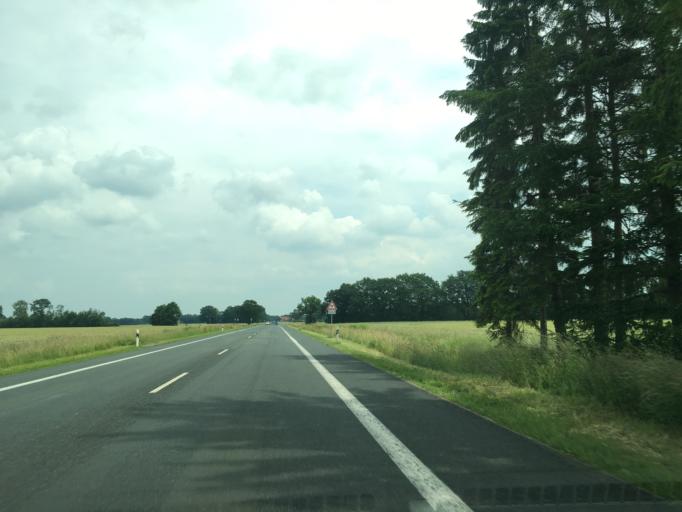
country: DE
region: North Rhine-Westphalia
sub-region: Regierungsbezirk Munster
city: Nordwalde
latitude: 52.1469
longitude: 7.4344
